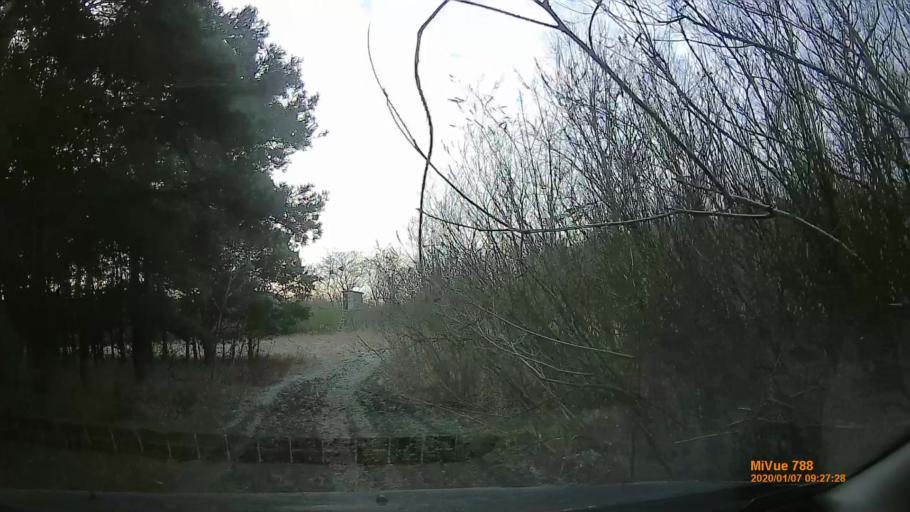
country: HU
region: Gyor-Moson-Sopron
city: Rajka
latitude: 47.9502
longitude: 17.1686
